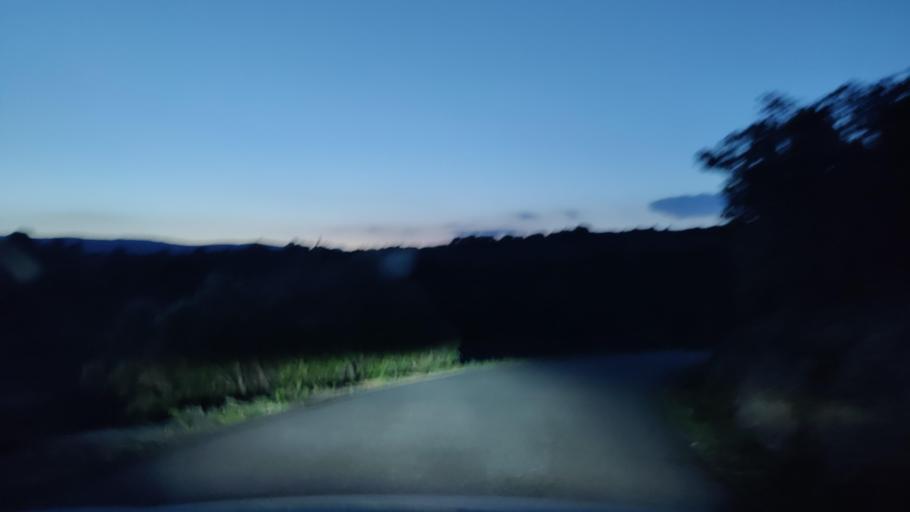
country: FR
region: Languedoc-Roussillon
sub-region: Departement des Pyrenees-Orientales
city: Estagel
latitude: 42.8820
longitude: 2.7480
